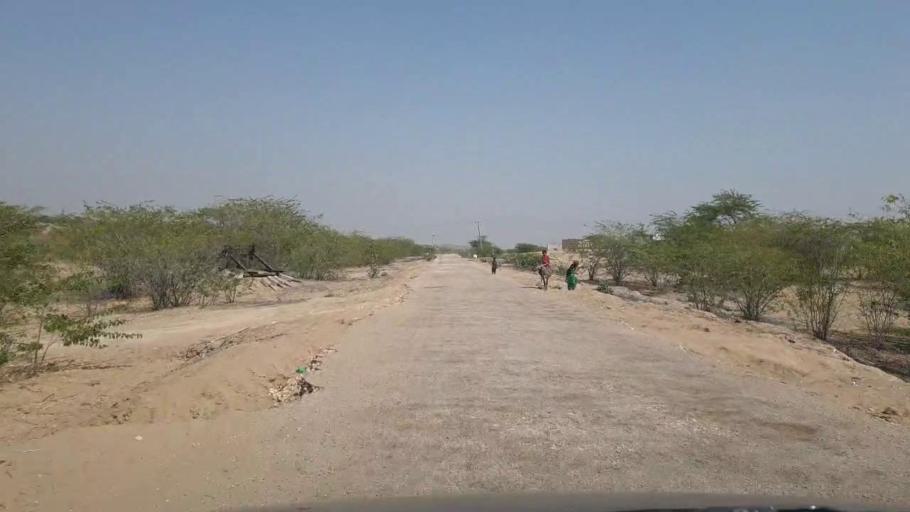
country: PK
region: Sindh
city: Chor
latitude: 25.6993
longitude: 70.1989
